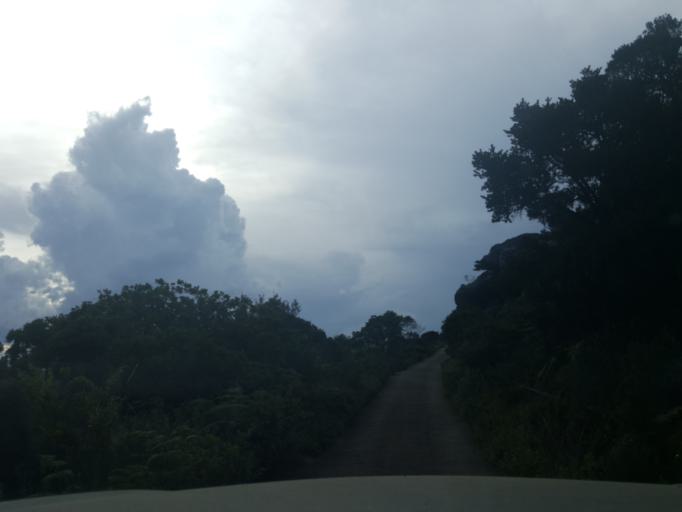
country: ZA
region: Limpopo
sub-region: Mopani District Municipality
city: Hoedspruit
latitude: -24.5481
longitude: 30.8678
